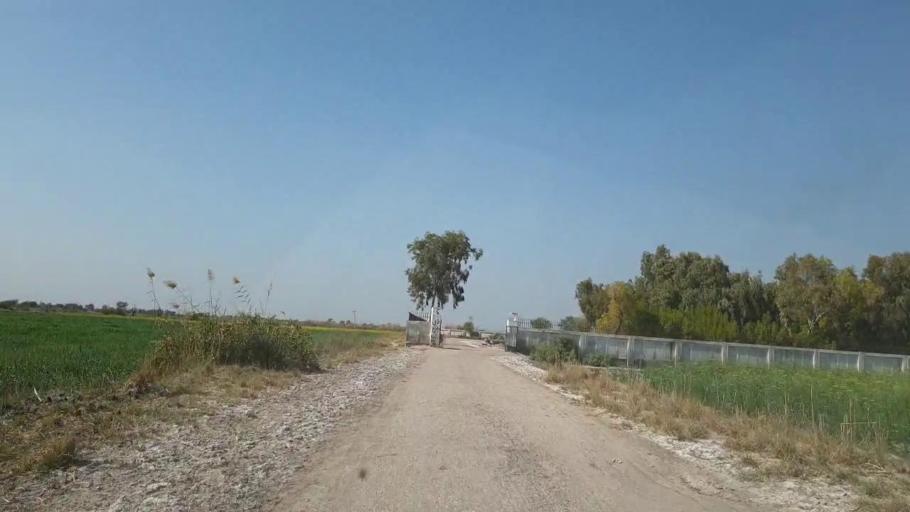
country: PK
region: Sindh
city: Mirpur Khas
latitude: 25.7186
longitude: 69.1298
